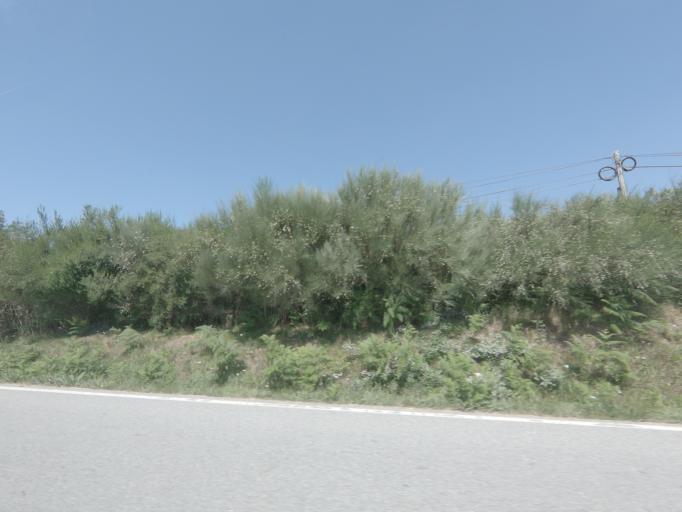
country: PT
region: Viseu
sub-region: Tarouca
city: Tarouca
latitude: 40.9976
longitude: -7.8851
